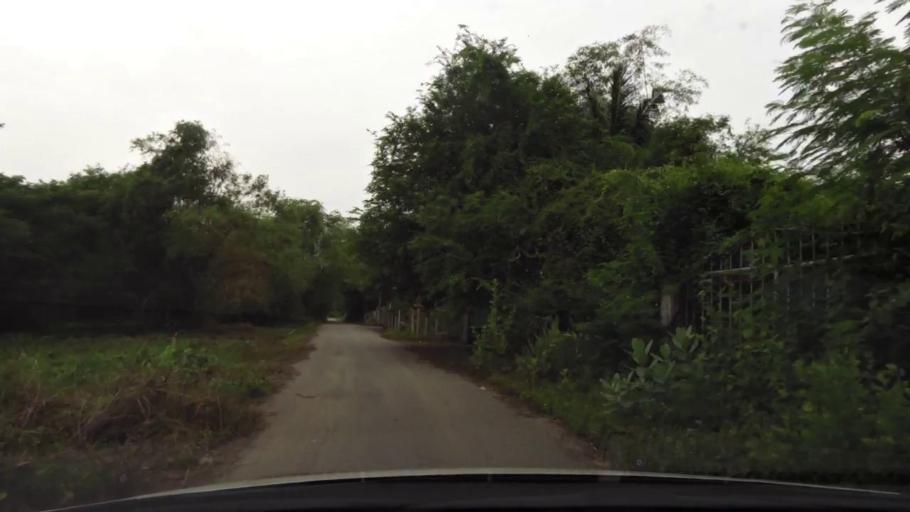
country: TH
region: Samut Sakhon
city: Ban Phaeo
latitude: 13.6045
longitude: 100.0078
